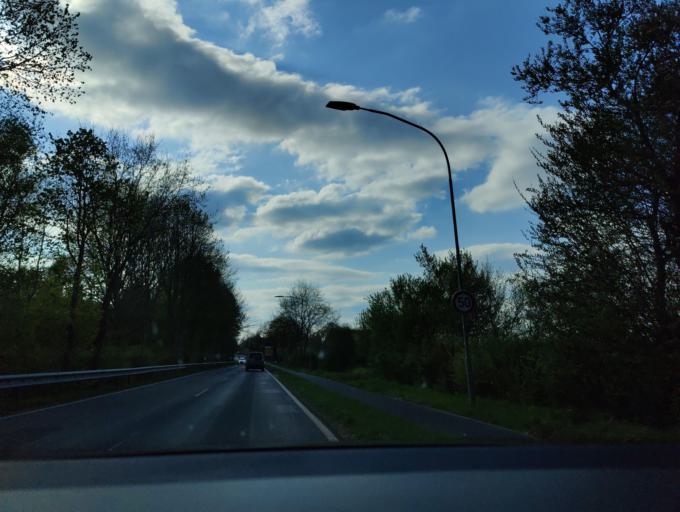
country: DE
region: Lower Saxony
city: Nordhorn
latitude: 52.4212
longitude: 7.0940
